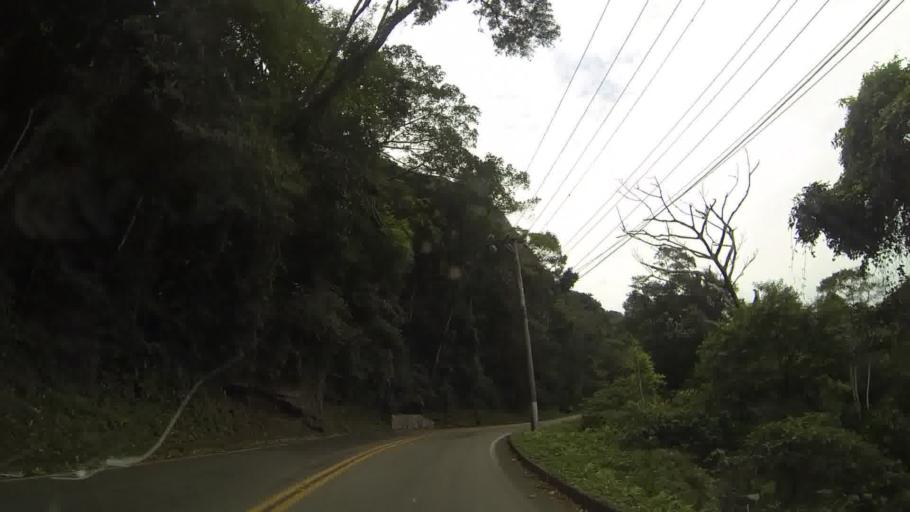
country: BR
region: Sao Paulo
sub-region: Sao Sebastiao
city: Sao Sebastiao
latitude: -23.8271
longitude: -45.4923
